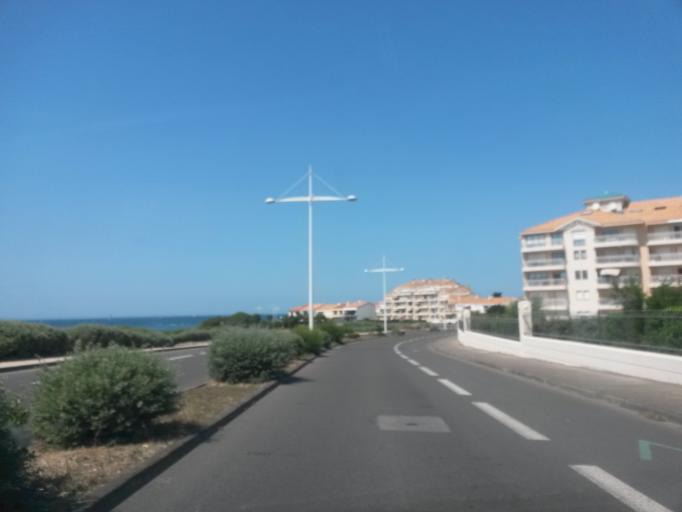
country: FR
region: Pays de la Loire
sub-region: Departement de la Vendee
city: Les Sables-d'Olonne
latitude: 46.4913
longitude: -1.8055
